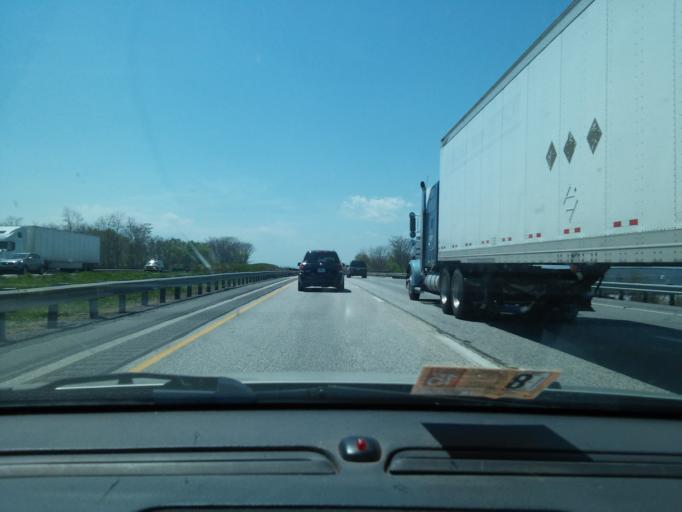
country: US
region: Pennsylvania
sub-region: Franklin County
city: Chambersburg
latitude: 39.9080
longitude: -77.6502
